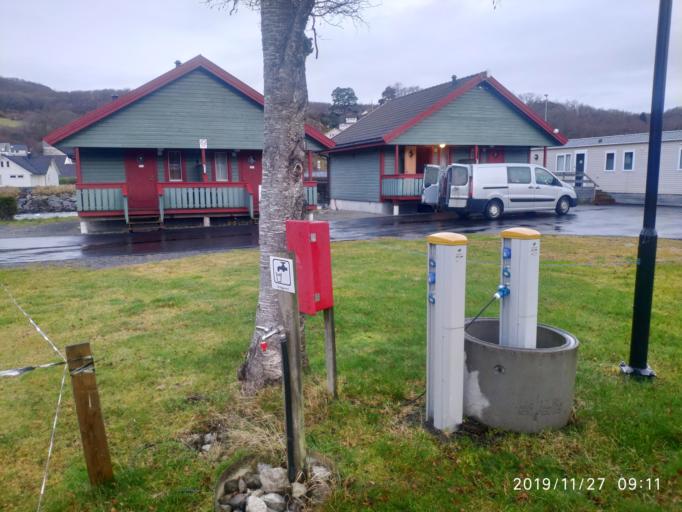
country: NO
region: Rogaland
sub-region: Eigersund
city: Egersund
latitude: 58.4792
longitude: 5.9964
